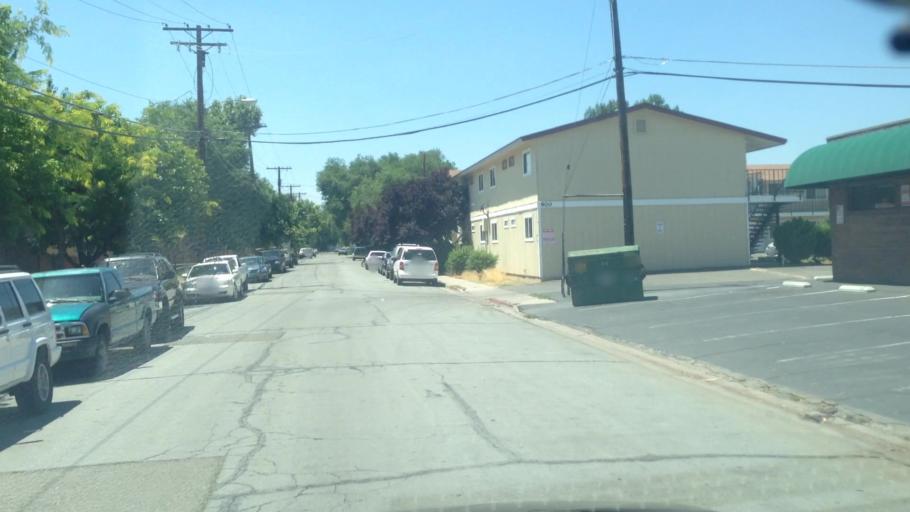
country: US
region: Nevada
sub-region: Washoe County
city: Sparks
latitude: 39.5431
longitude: -119.7539
